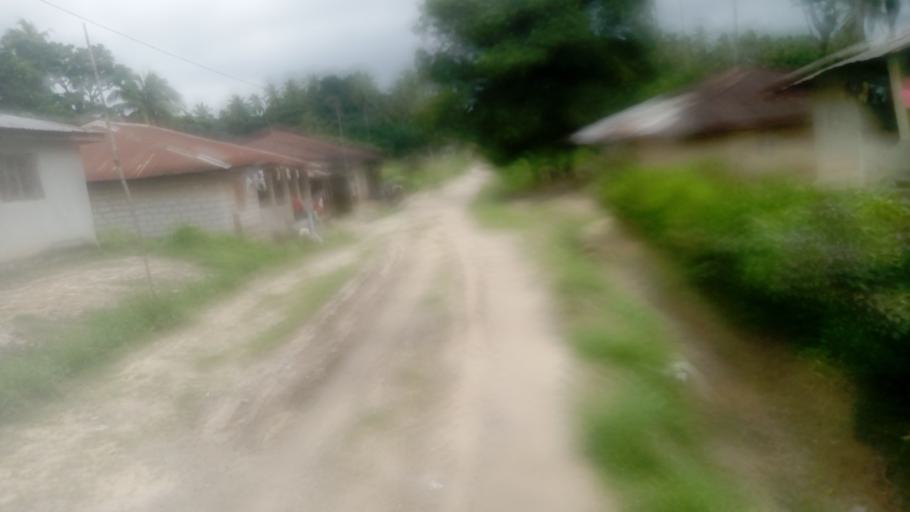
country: SL
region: Northern Province
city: Lunsar
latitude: 8.6795
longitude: -12.5376
